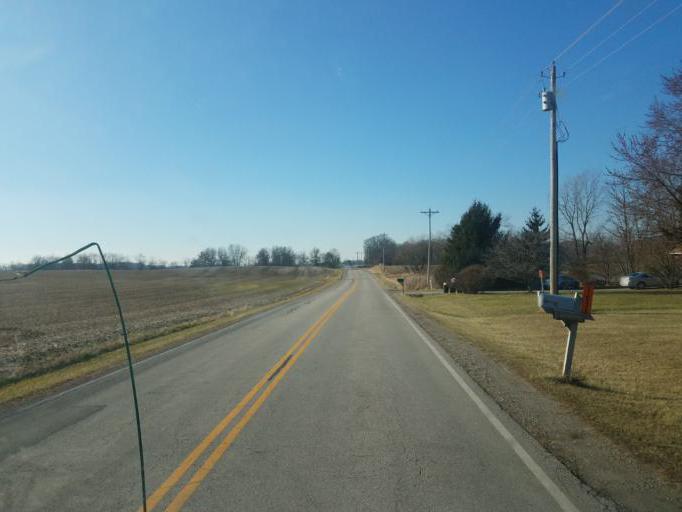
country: US
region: Ohio
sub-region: Marion County
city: Marion
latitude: 40.6442
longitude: -83.1765
